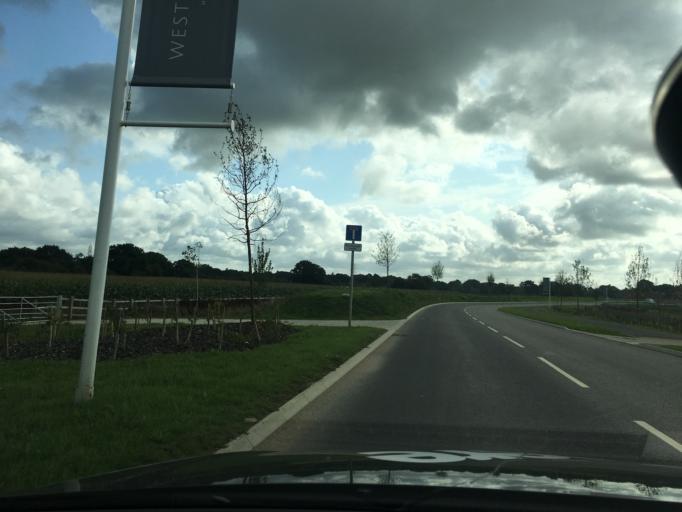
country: GB
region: England
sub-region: Surrey
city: Salfords
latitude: 51.1891
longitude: -0.1909
